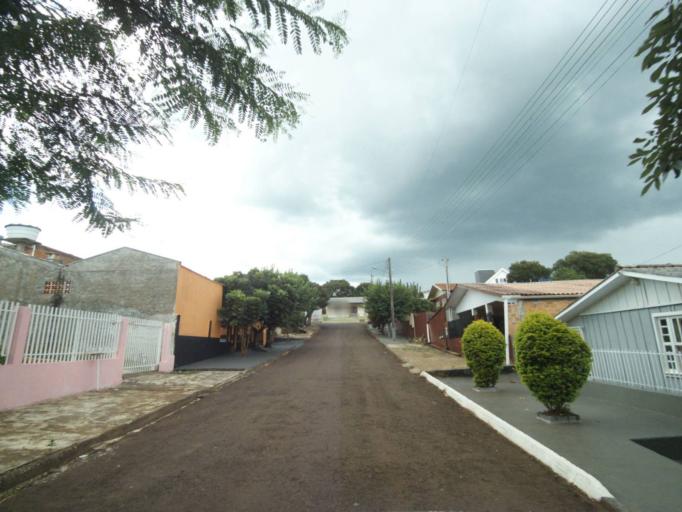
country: BR
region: Parana
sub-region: Guaraniacu
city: Guaraniacu
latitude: -25.0961
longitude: -52.8709
